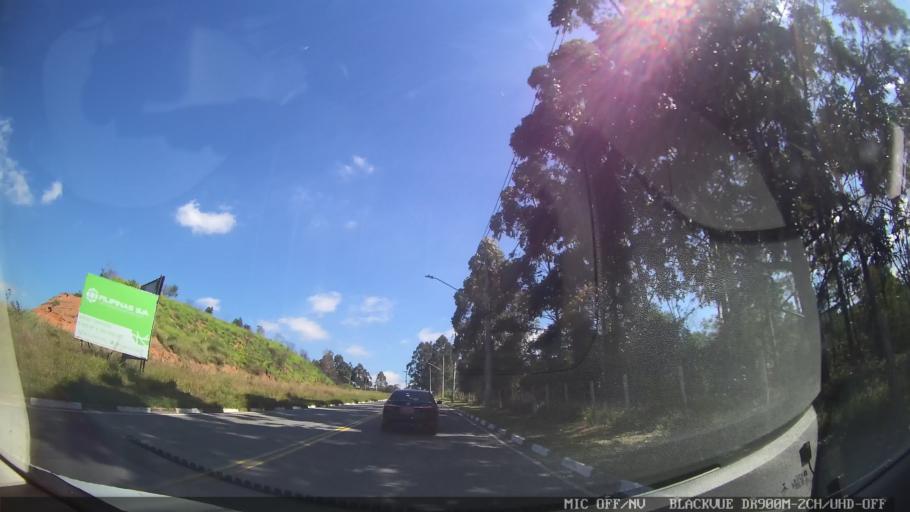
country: BR
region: Sao Paulo
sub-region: Barueri
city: Barueri
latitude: -23.4442
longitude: -46.8351
